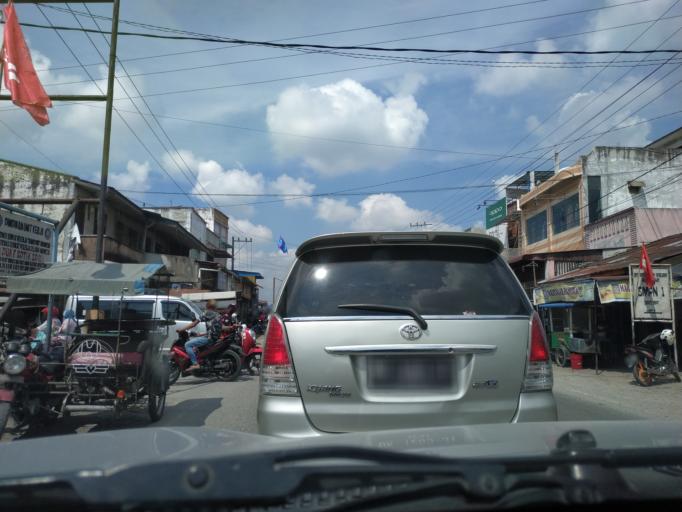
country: ID
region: North Sumatra
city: Tanjungbalai
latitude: 2.9212
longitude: 99.7276
